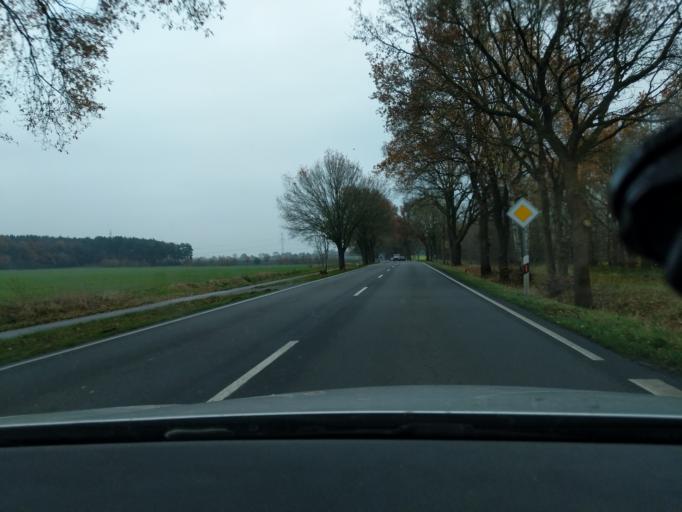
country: DE
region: Lower Saxony
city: Gyhum
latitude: 53.2308
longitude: 9.2881
